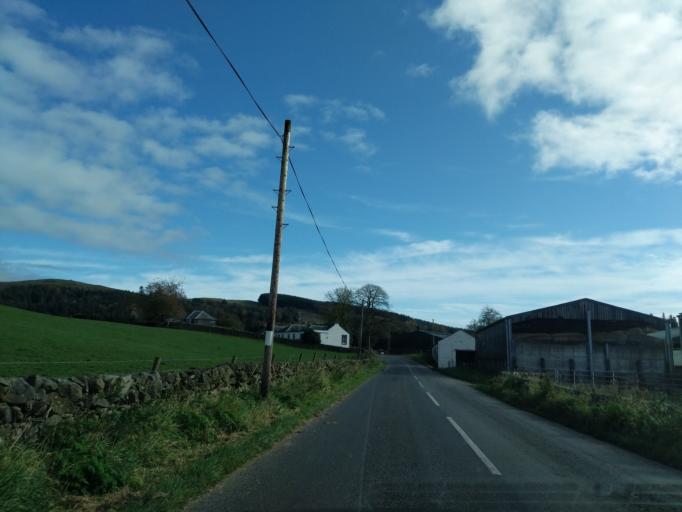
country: GB
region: Scotland
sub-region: Dumfries and Galloway
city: Thornhill
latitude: 55.1913
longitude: -3.8588
